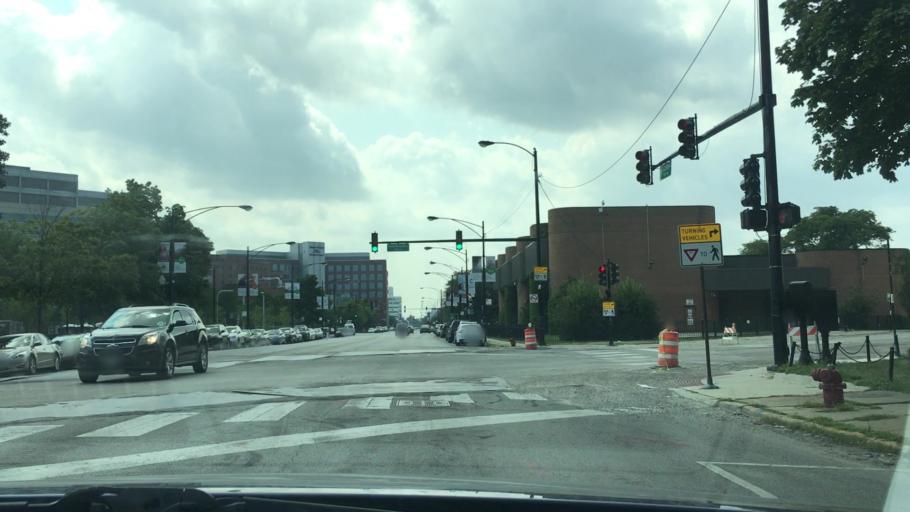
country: US
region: Illinois
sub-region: Cook County
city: Chicago
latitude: 41.8742
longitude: -87.6748
